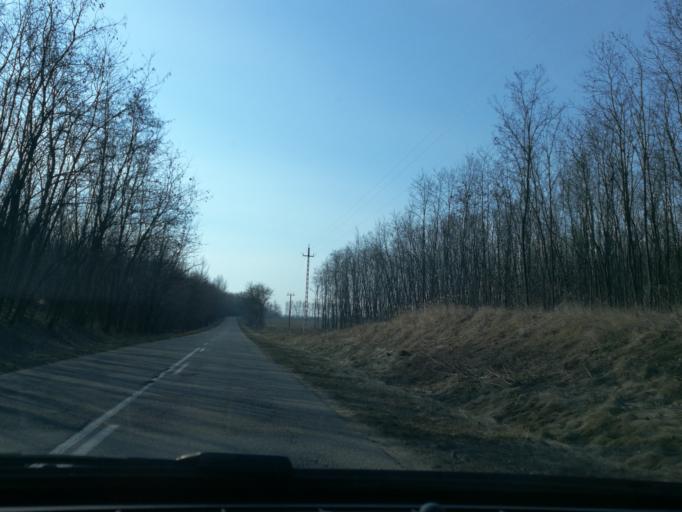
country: HU
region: Szabolcs-Szatmar-Bereg
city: Levelek
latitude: 47.9947
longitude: 21.9672
